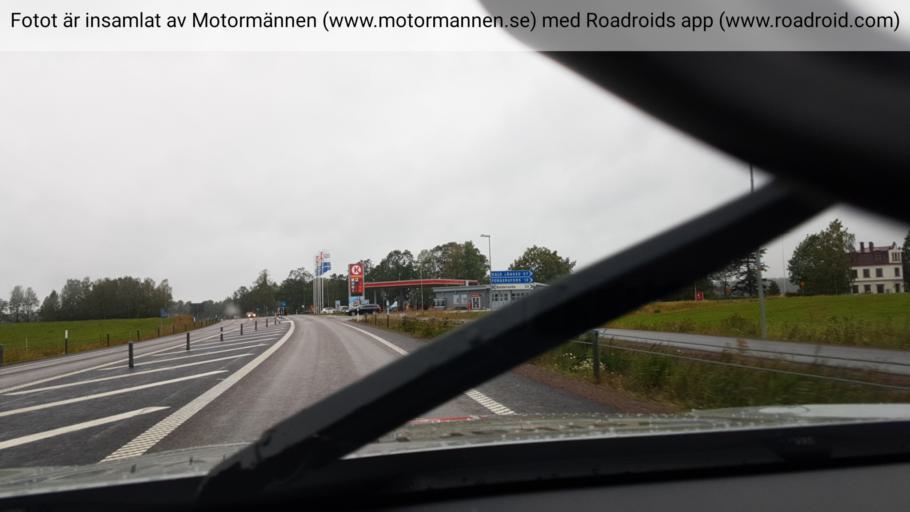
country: SE
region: Vaestra Goetaland
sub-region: Amals Kommun
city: Amal
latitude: 58.9751
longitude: 12.6261
